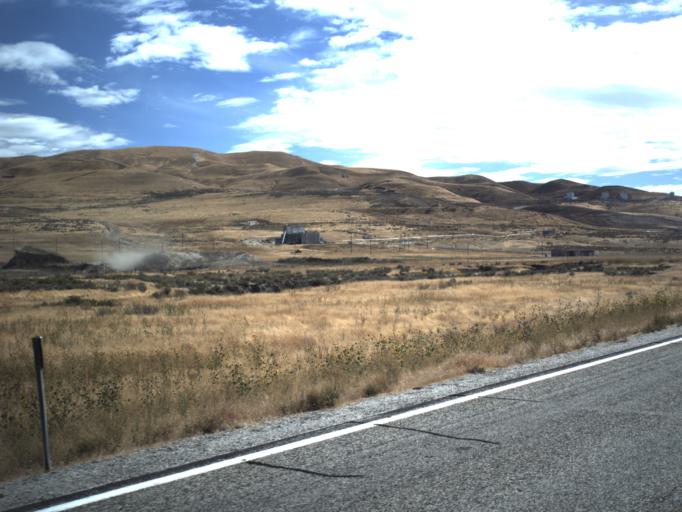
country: US
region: Utah
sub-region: Box Elder County
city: Tremonton
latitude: 41.6969
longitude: -112.4456
